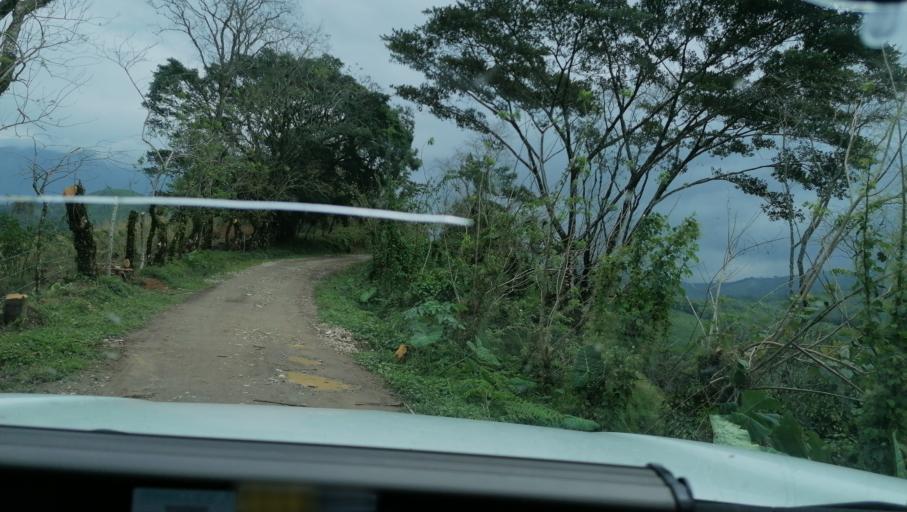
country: MX
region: Chiapas
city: Ixtacomitan
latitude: 17.3465
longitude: -93.1400
